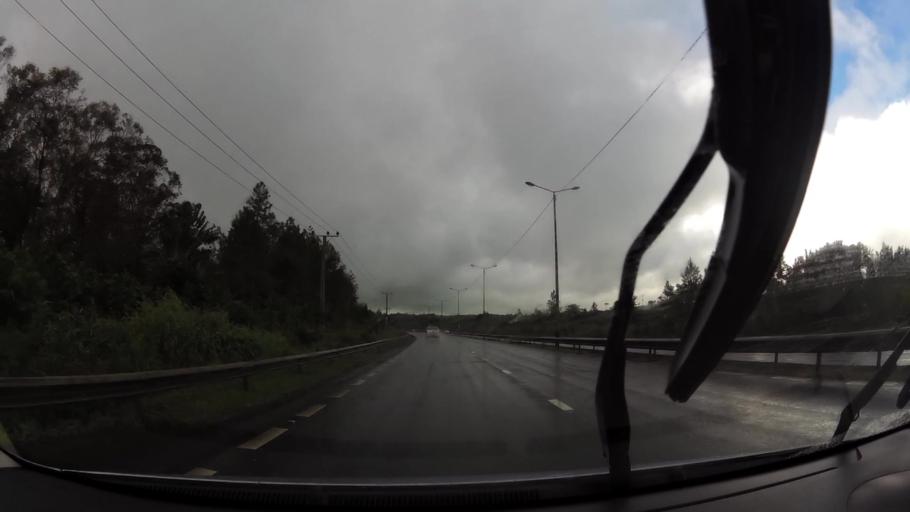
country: MU
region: Plaines Wilhems
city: Midlands
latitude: -20.3235
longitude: 57.5433
